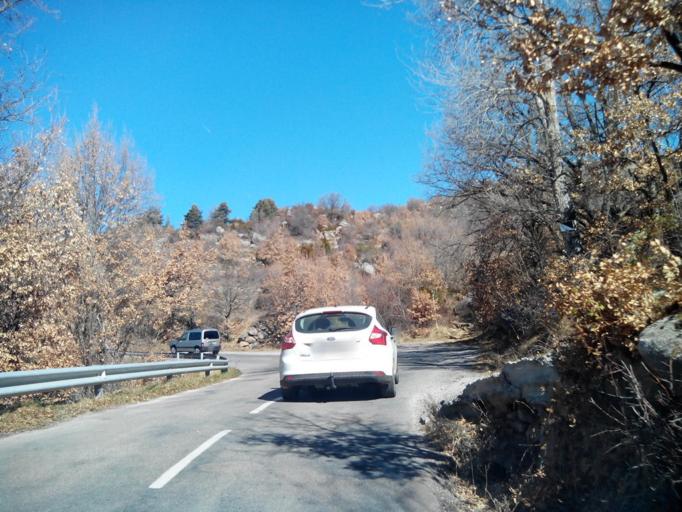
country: ES
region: Catalonia
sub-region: Provincia de Lleida
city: Lles de Cerdanya
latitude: 42.3802
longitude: 1.6868
